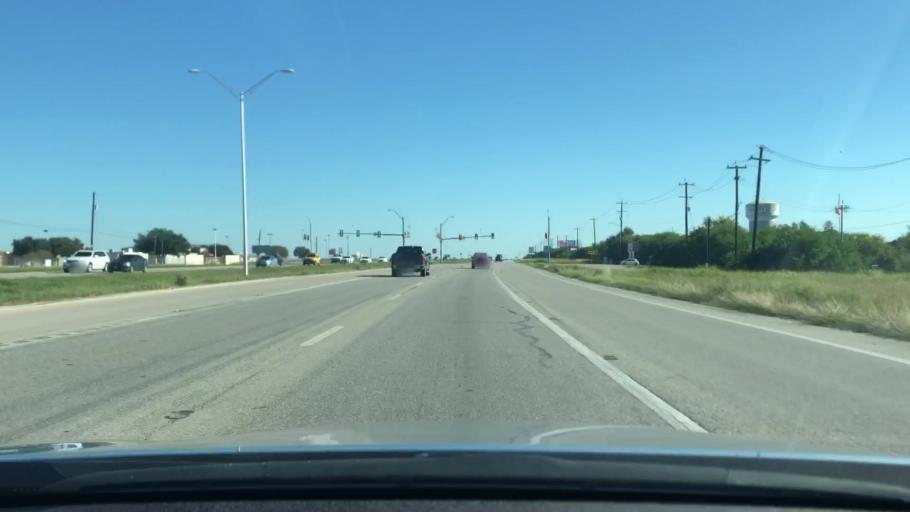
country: US
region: Texas
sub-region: Bexar County
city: Universal City
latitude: 29.5290
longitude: -98.2985
